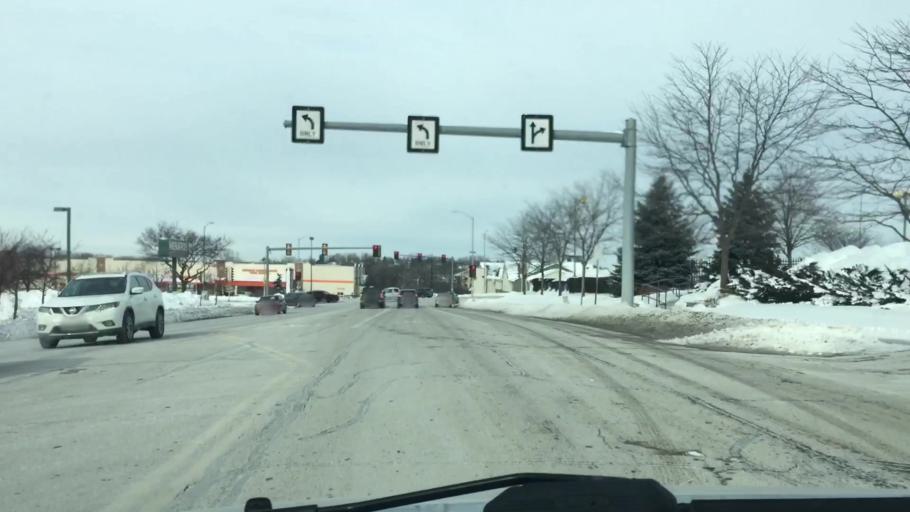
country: US
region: Wisconsin
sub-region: Waukesha County
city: Waukesha
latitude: 43.0353
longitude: -88.1792
